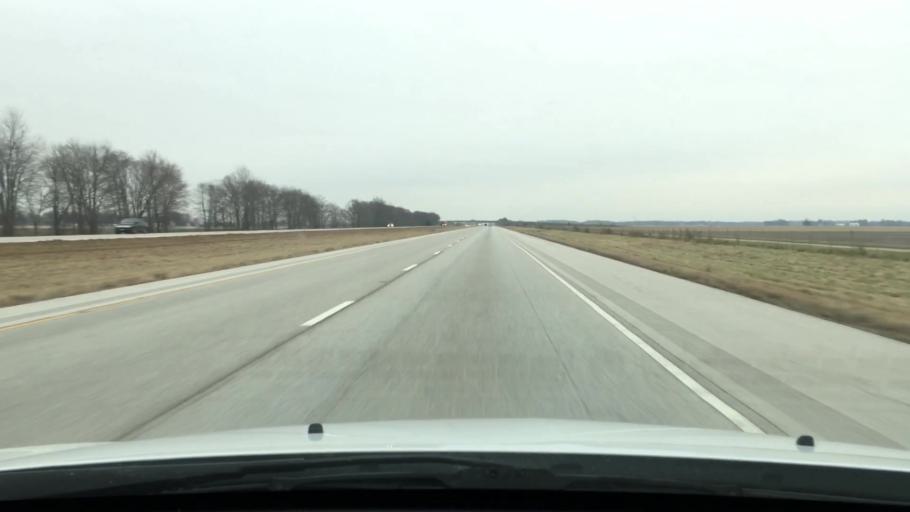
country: US
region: Illinois
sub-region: Scott County
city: Winchester
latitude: 39.6801
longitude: -90.3609
